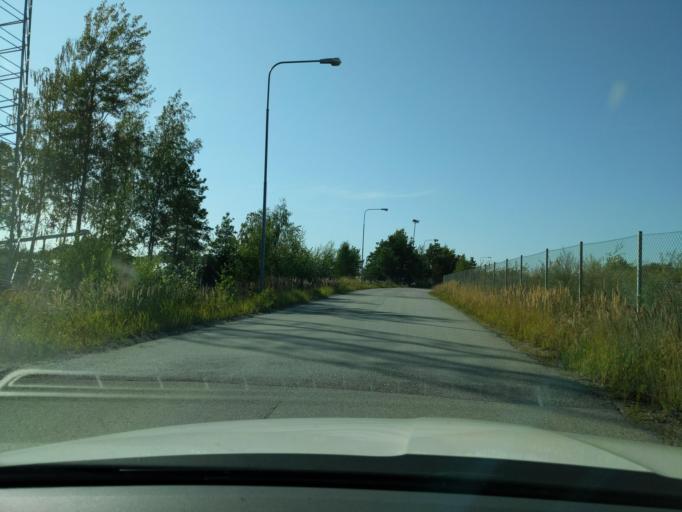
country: FI
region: Uusimaa
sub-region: Raaseporin
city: Inga
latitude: 60.0180
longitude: 23.9252
